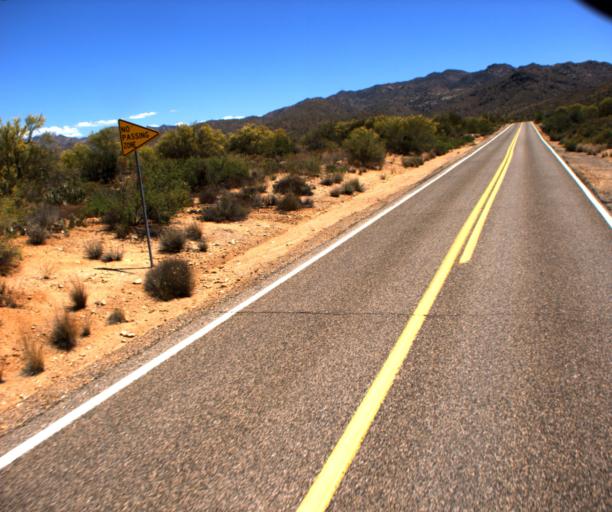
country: US
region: Arizona
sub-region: Yavapai County
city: Bagdad
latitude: 34.4654
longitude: -113.0453
